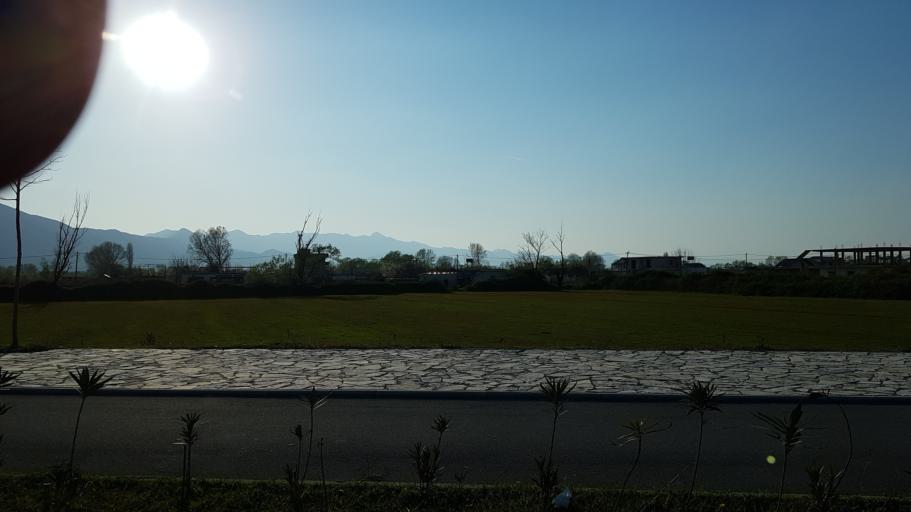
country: AL
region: Shkoder
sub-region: Rrethi i Shkodres
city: Shkoder
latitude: 42.0771
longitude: 19.4915
